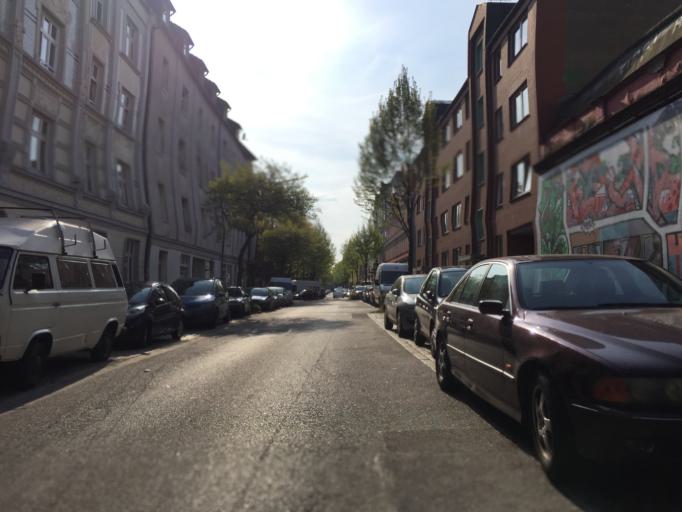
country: DE
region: Hamburg
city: Kleiner Grasbrook
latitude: 53.5184
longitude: 9.9838
